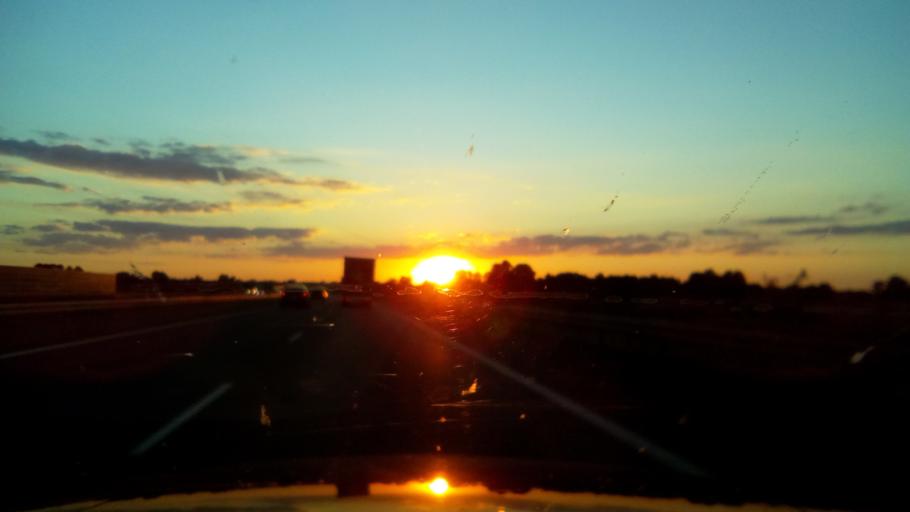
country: PL
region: Lodz Voivodeship
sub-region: Powiat poddebicki
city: Dalikow
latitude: 51.9639
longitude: 19.1159
